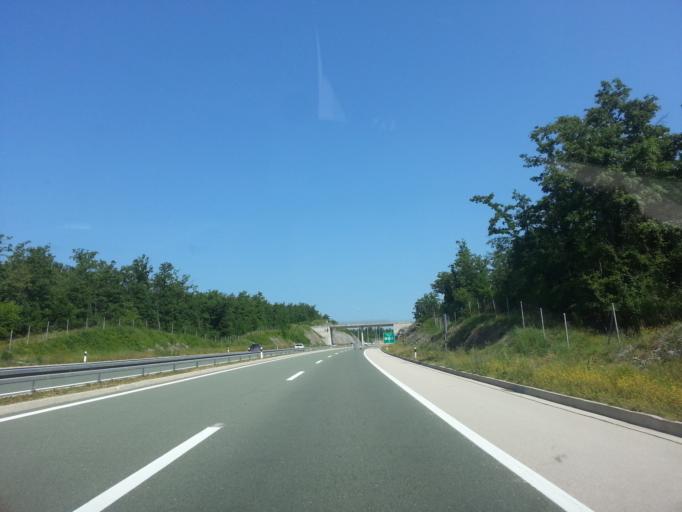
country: HR
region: Primorsko-Goranska
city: Matulji
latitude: 45.4381
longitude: 14.2776
